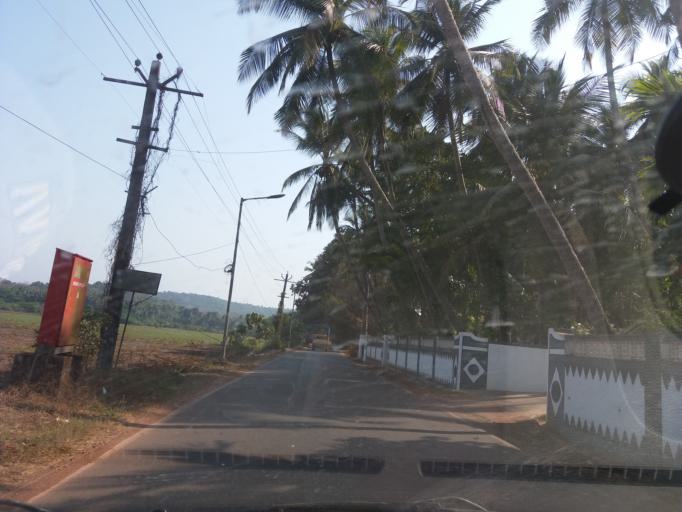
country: IN
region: Goa
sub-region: North Goa
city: Queula
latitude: 15.3482
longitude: 73.9795
